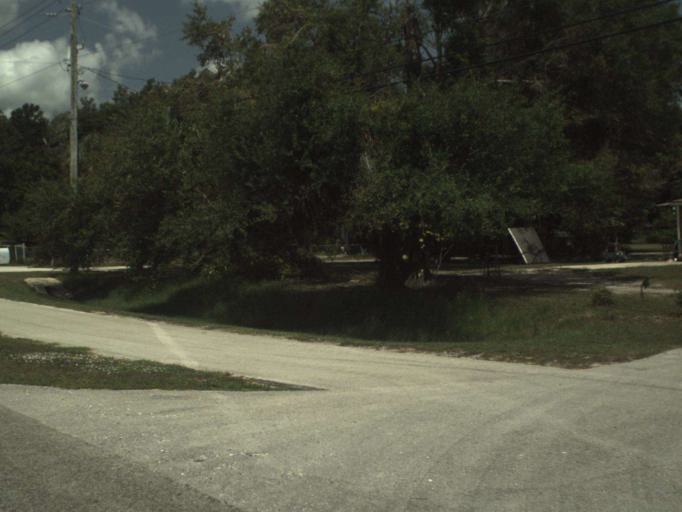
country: US
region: Florida
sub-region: Saint Lucie County
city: Fort Pierce South
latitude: 27.4029
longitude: -80.4426
